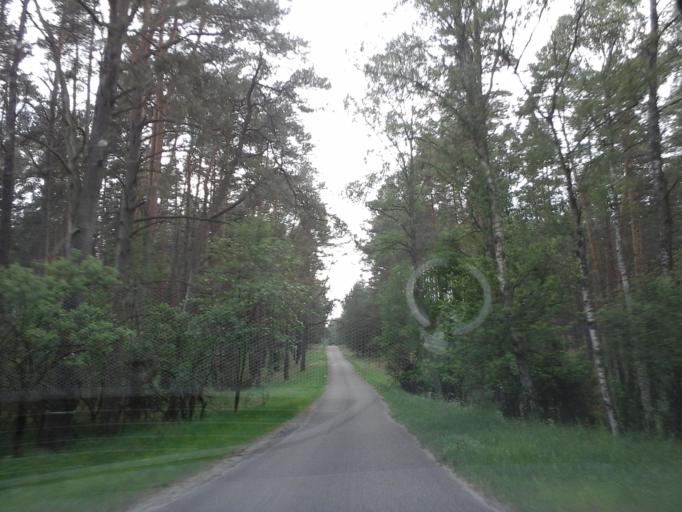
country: PL
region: West Pomeranian Voivodeship
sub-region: Powiat walecki
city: Tuczno
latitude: 53.2308
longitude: 16.0828
